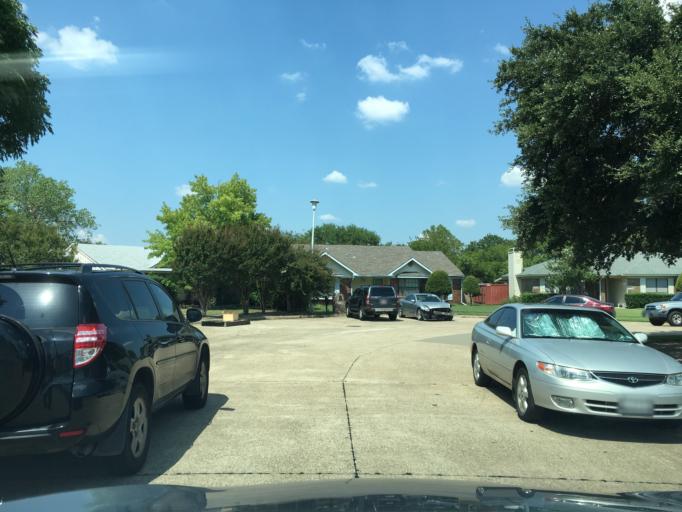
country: US
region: Texas
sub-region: Dallas County
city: Garland
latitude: 32.9498
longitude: -96.6638
